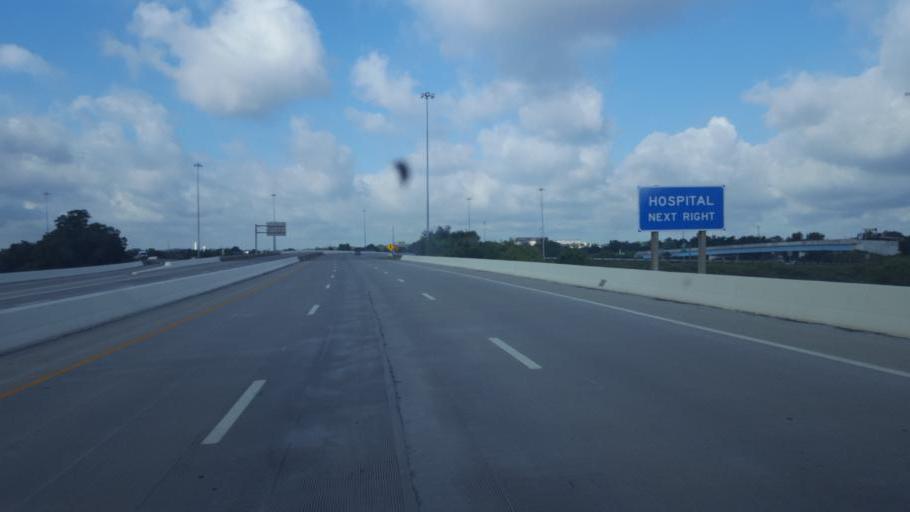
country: US
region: Ohio
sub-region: Stark County
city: Canton
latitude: 40.7866
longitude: -81.3820
